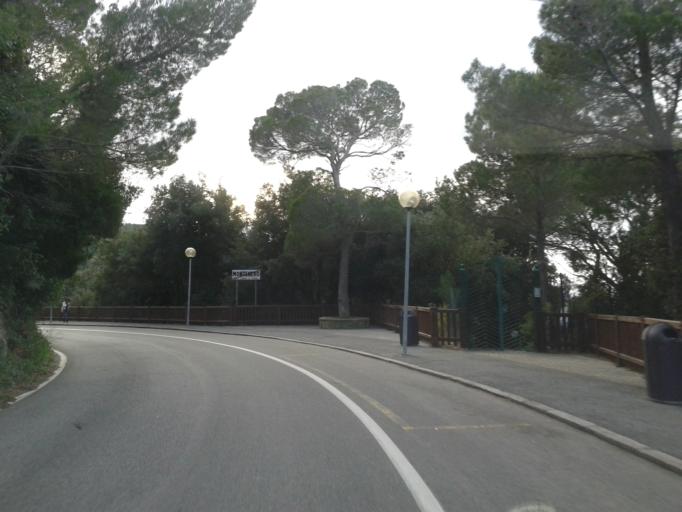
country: IT
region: Tuscany
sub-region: Provincia di Livorno
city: Quercianella
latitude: 43.4925
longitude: 10.3464
